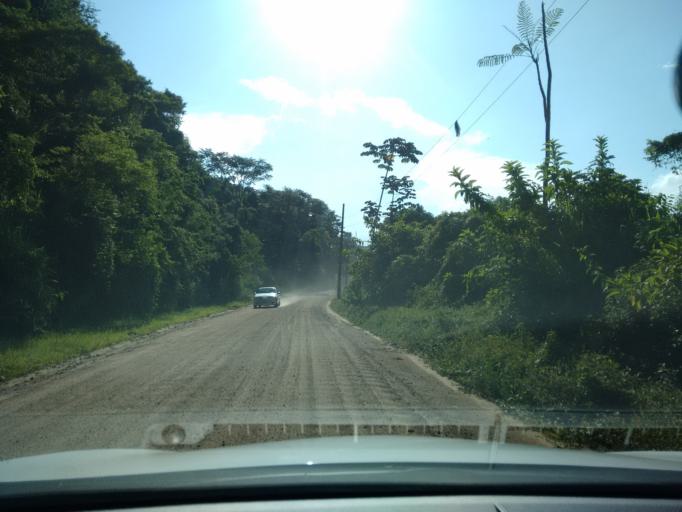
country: BR
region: Santa Catarina
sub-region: Blumenau
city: Blumenau
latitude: -26.8991
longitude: -49.0723
